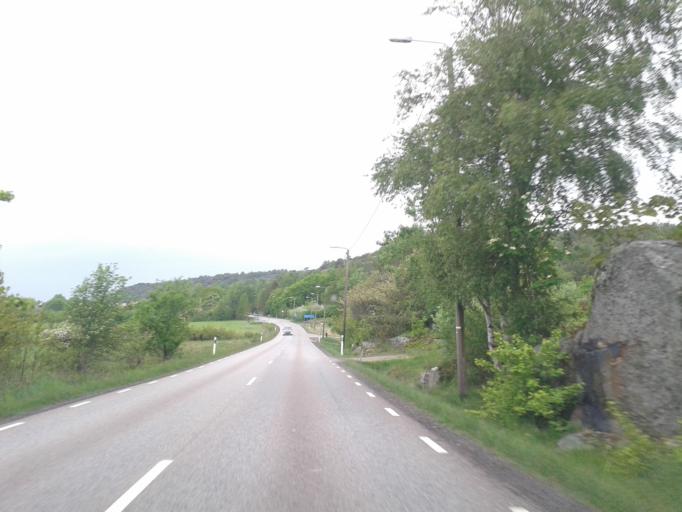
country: SE
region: Vaestra Goetaland
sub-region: Kungalvs Kommun
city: Kode
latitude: 57.8967
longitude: 11.7344
